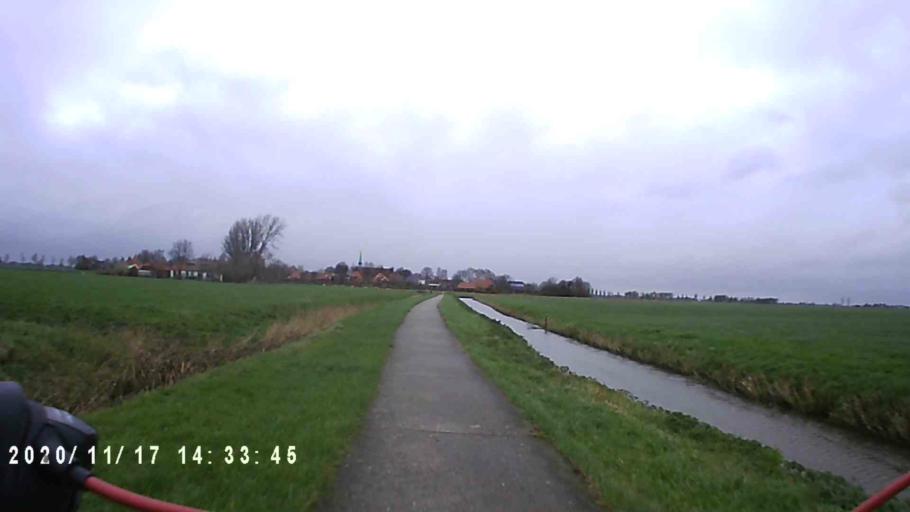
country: NL
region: Groningen
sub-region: Gemeente Zuidhorn
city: Oldehove
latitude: 53.2869
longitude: 6.3647
